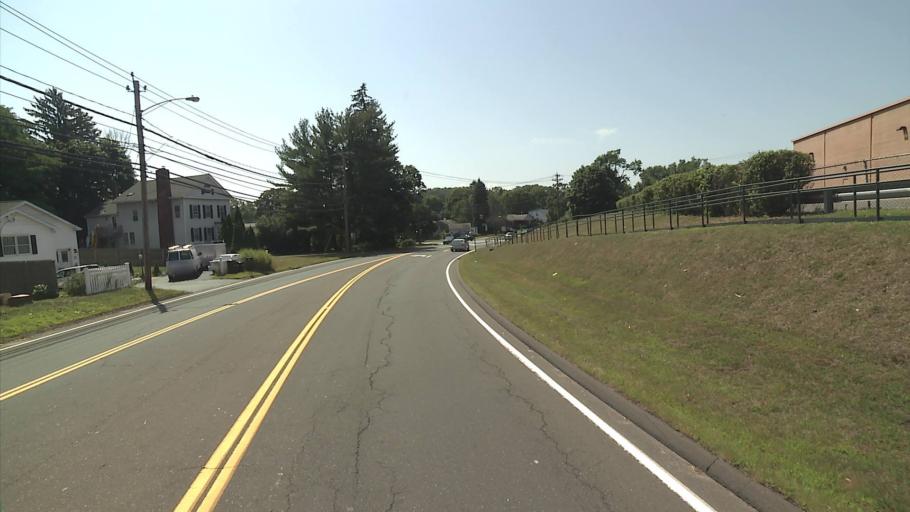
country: US
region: Connecticut
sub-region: New Haven County
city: Branford Center
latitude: 41.2731
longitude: -72.8298
